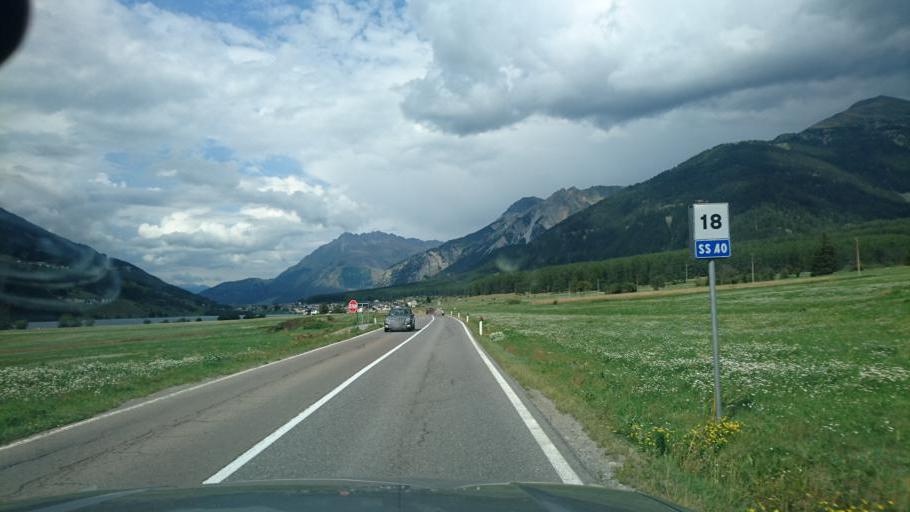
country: IT
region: Trentino-Alto Adige
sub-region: Bolzano
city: Malles Venosta
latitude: 46.7423
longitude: 10.5347
